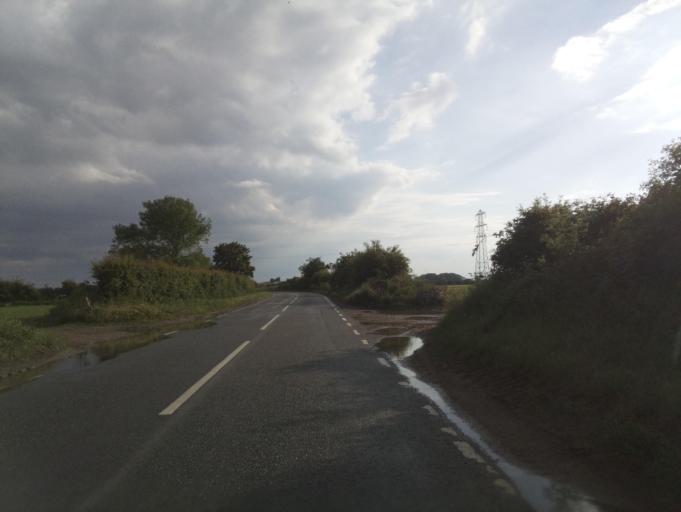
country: GB
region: England
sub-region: Lincolnshire
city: Great Gonerby
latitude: 52.9749
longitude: -0.6820
